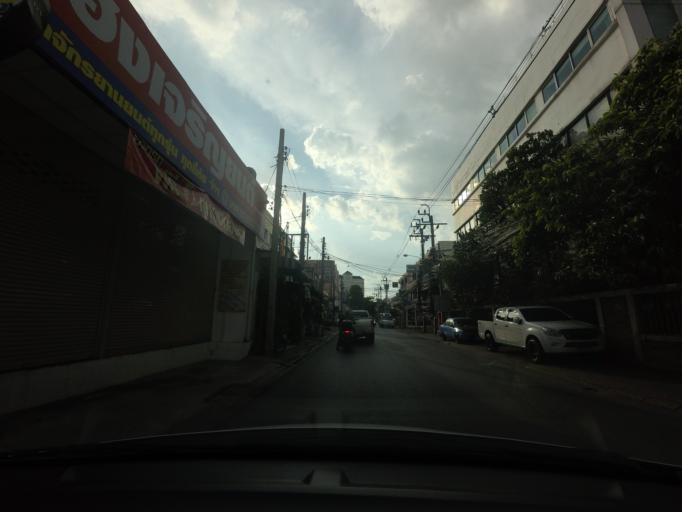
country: TH
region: Bangkok
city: Lak Si
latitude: 13.8909
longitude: 100.5812
